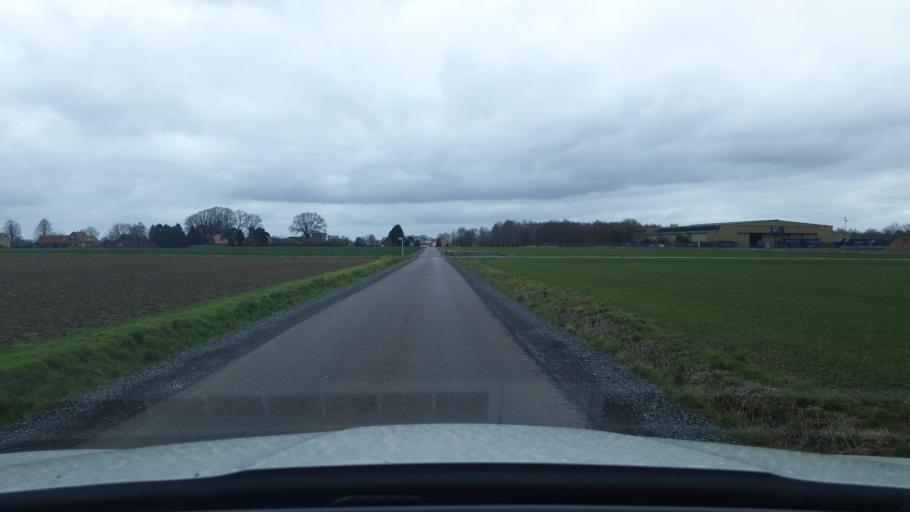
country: DE
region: North Rhine-Westphalia
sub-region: Regierungsbezirk Detmold
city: Minden
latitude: 52.3187
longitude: 8.8522
